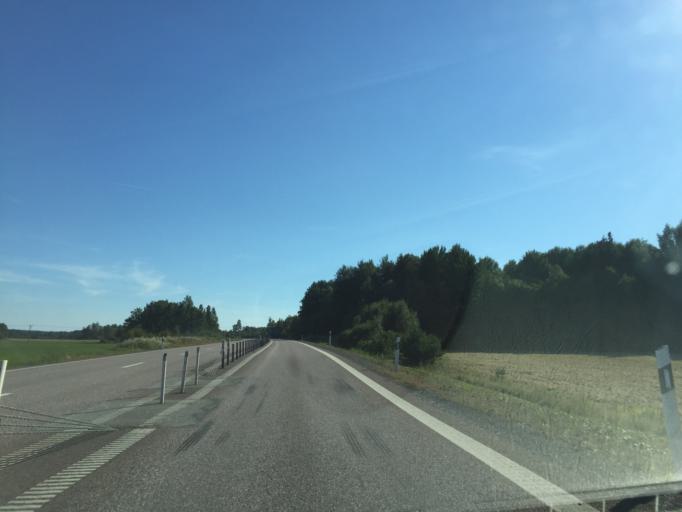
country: SE
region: Vaestmanland
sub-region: Arboga Kommun
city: Arboga
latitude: 59.4200
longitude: 15.8862
